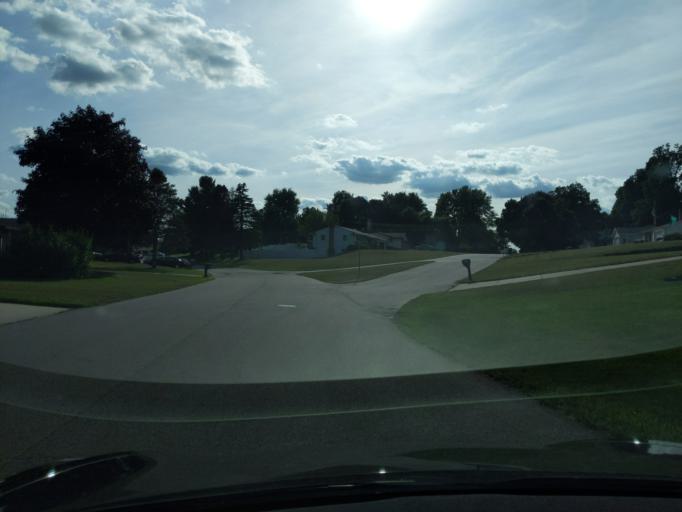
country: US
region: Michigan
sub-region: Eaton County
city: Waverly
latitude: 42.7255
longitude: -84.6640
